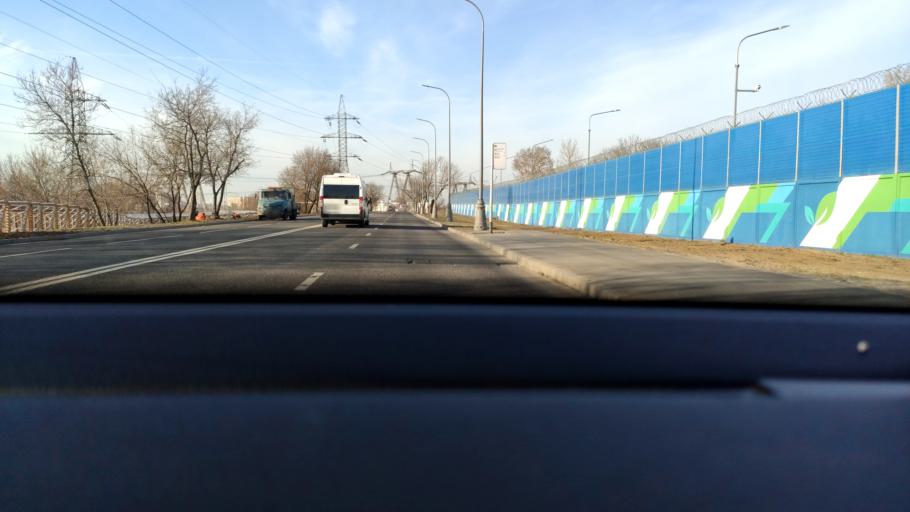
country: RU
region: Moscow
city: Kapotnya
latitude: 55.6488
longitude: 37.7891
